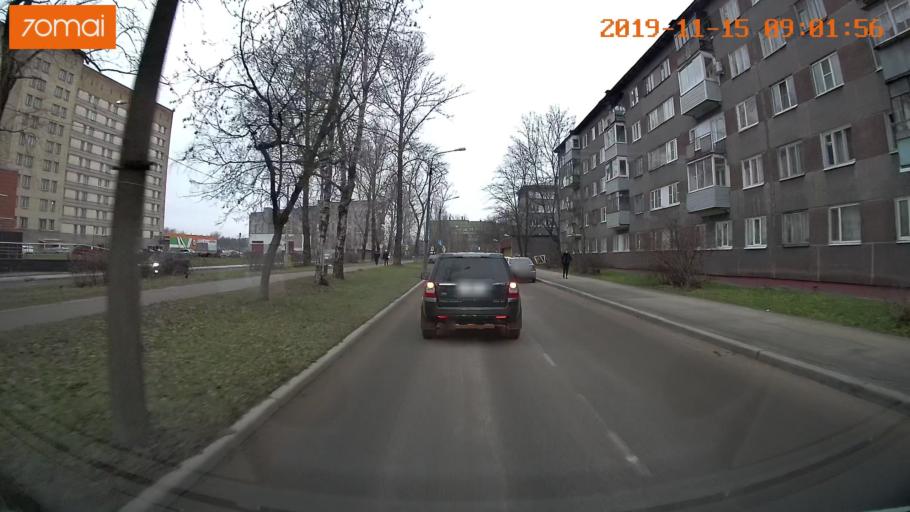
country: RU
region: Vologda
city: Cherepovets
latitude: 59.1347
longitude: 37.9270
